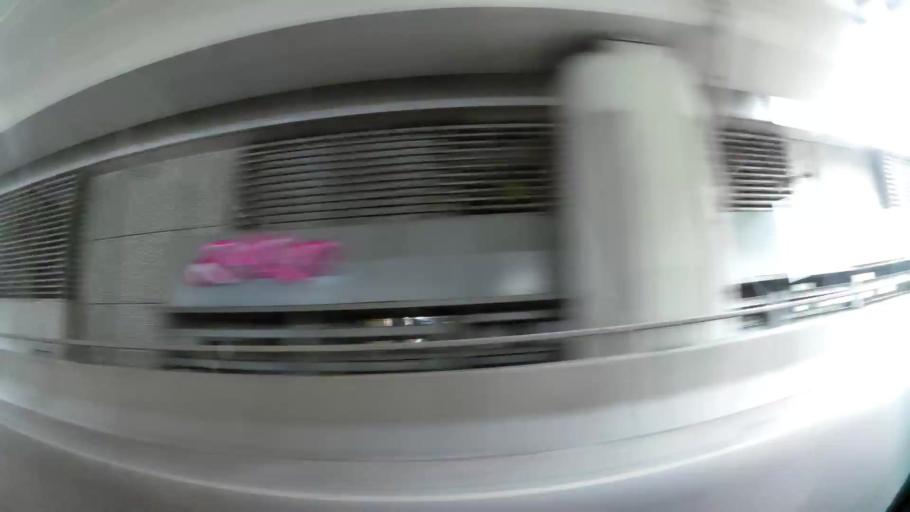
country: HK
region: Kowloon City
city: Kowloon
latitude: 22.3023
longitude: 114.1838
